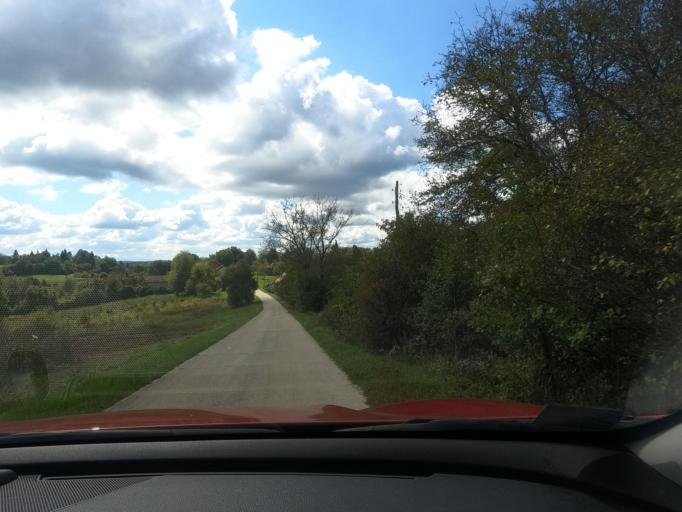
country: HR
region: Karlovacka
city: Vojnic
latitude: 45.2385
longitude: 15.7082
